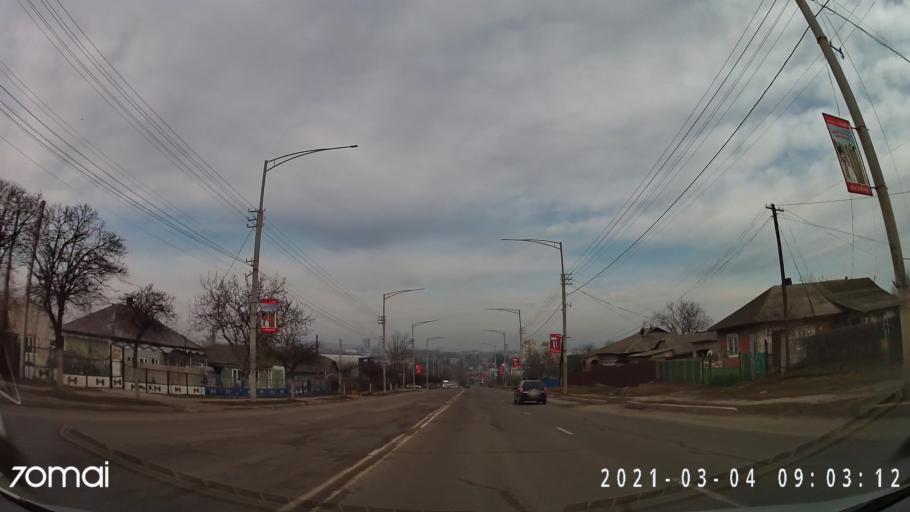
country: MD
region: Balti
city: Balti
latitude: 47.7476
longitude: 27.9466
